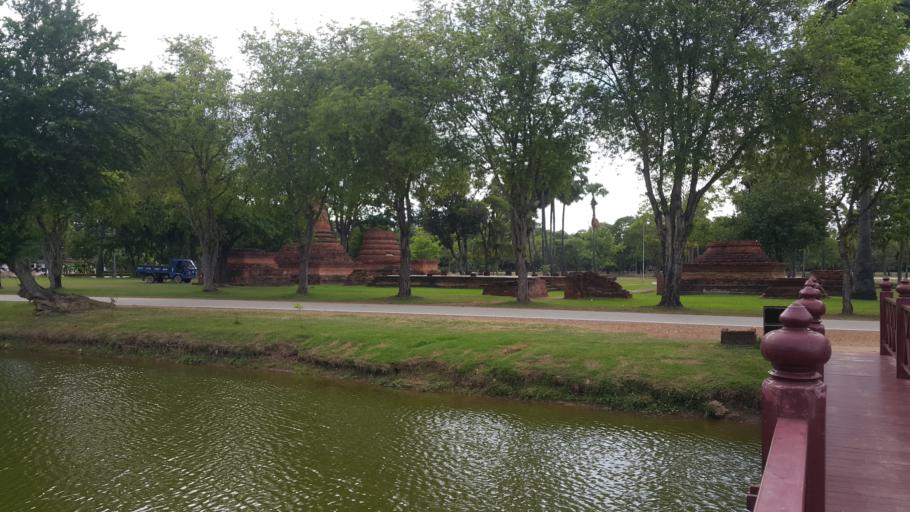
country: TH
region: Sukhothai
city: Ban Na
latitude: 17.0173
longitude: 99.7012
